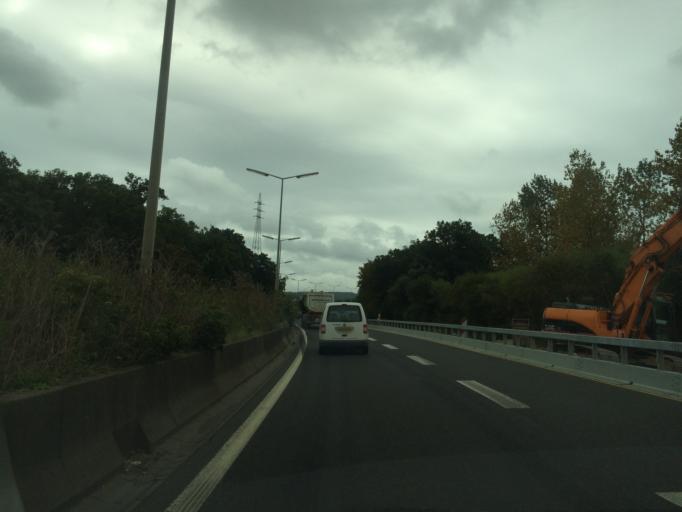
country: LU
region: Luxembourg
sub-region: Canton d'Esch-sur-Alzette
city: Esch-sur-Alzette
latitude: 49.5159
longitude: 5.9737
